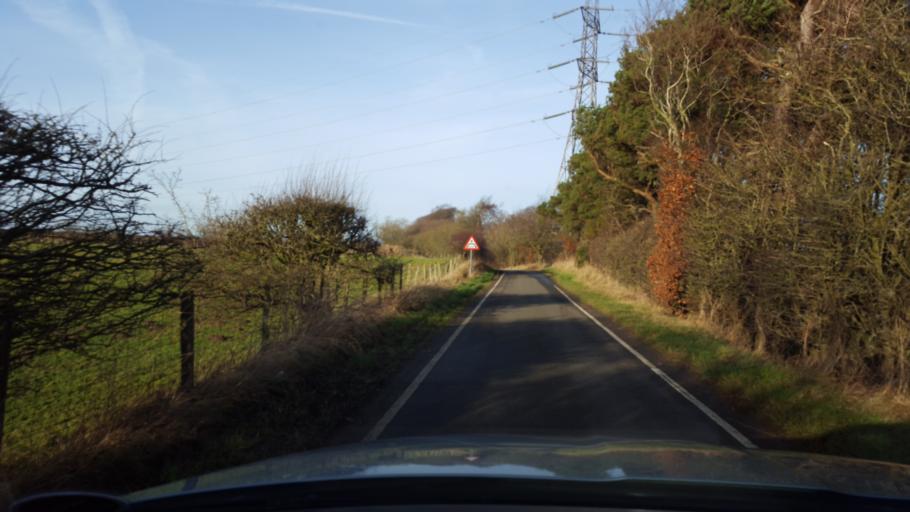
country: GB
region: Scotland
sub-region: West Lothian
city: Mid Calder
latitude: 55.8512
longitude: -3.5064
